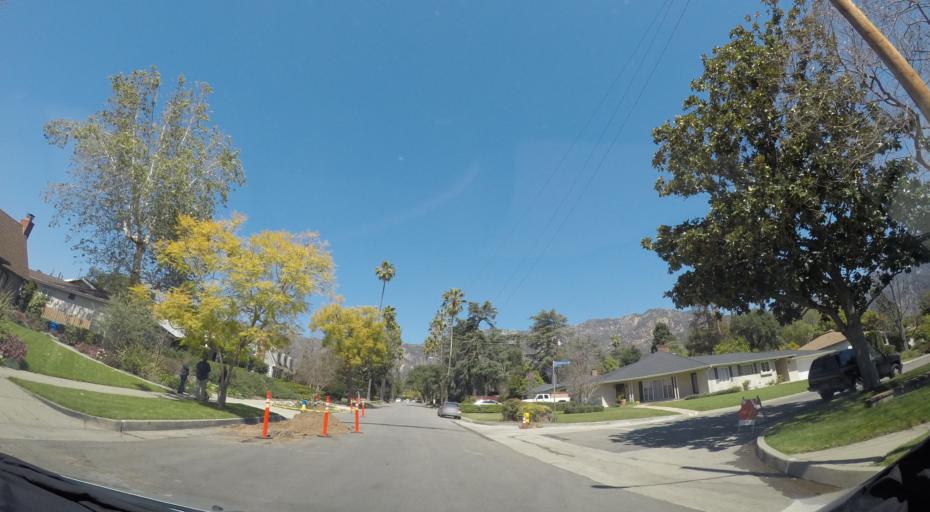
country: US
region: California
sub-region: Los Angeles County
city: Altadena
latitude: 34.1826
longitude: -118.1274
